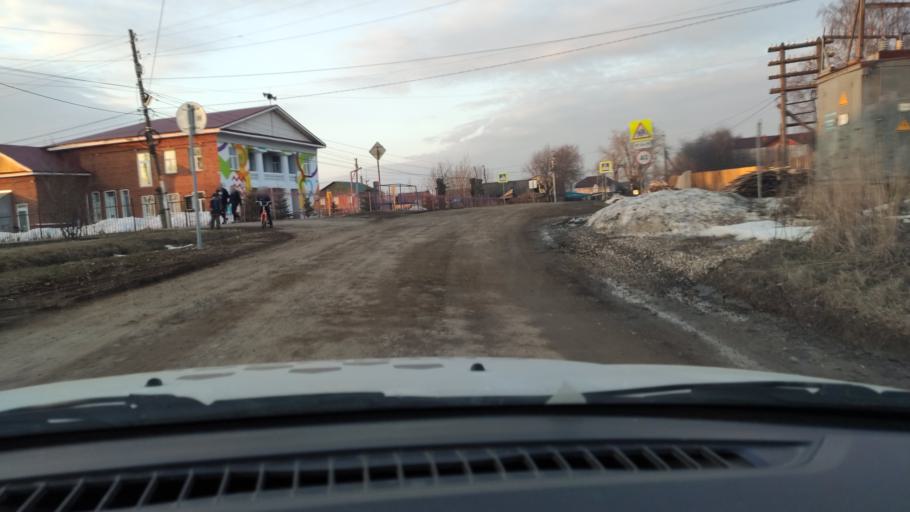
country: RU
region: Perm
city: Kultayevo
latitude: 57.9311
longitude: 56.0166
